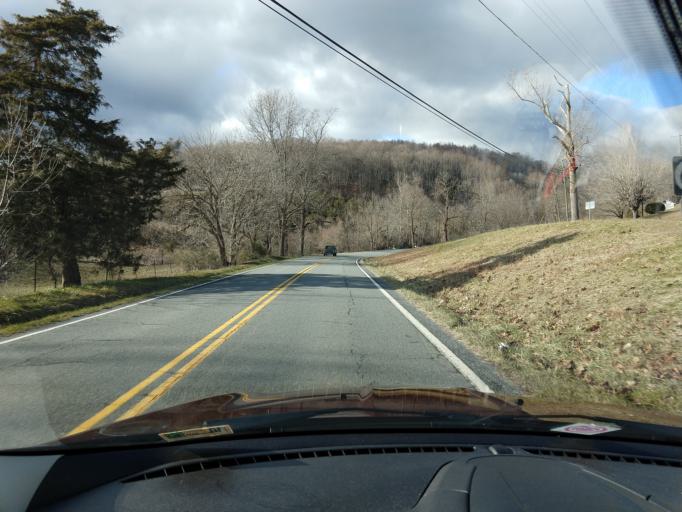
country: US
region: Virginia
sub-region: City of Lexington
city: Lexington
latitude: 37.8217
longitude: -79.4946
